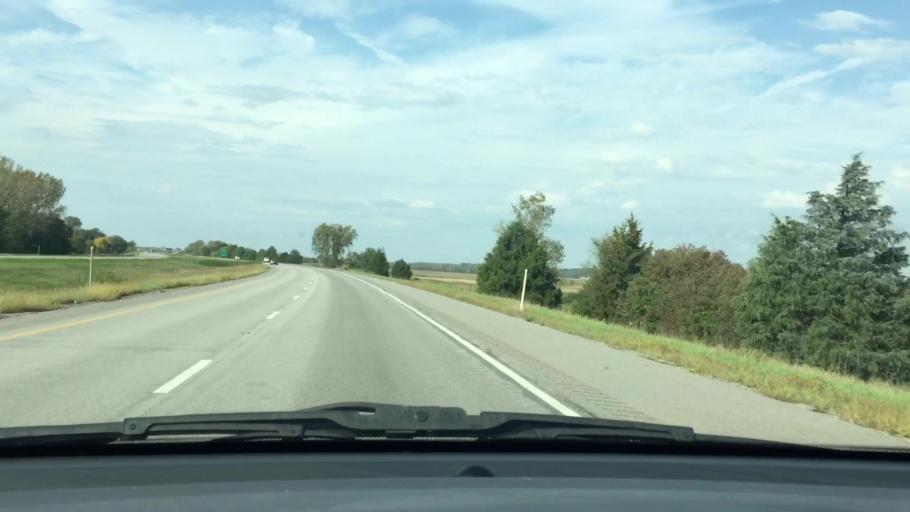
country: US
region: Iowa
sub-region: Scott County
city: Le Claire
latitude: 41.5415
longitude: -90.2832
